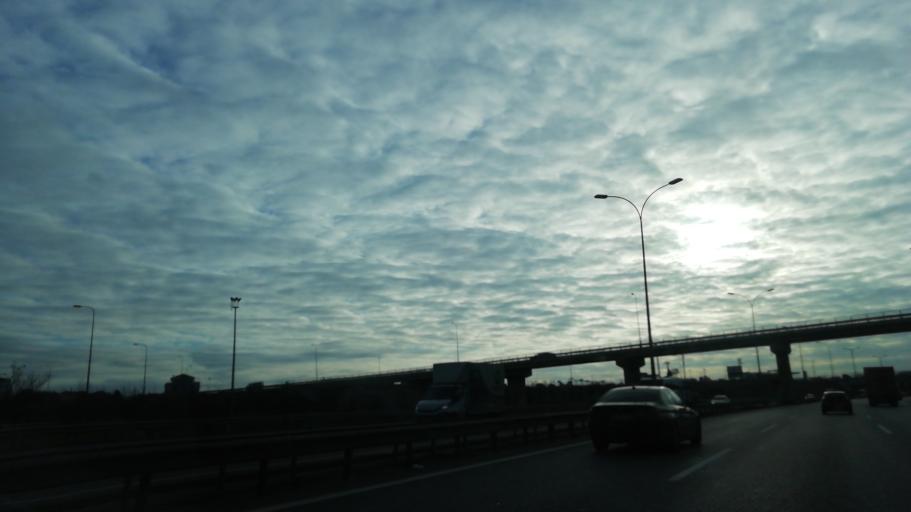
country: TR
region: Istanbul
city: Sultanbeyli
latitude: 40.9294
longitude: 29.3467
